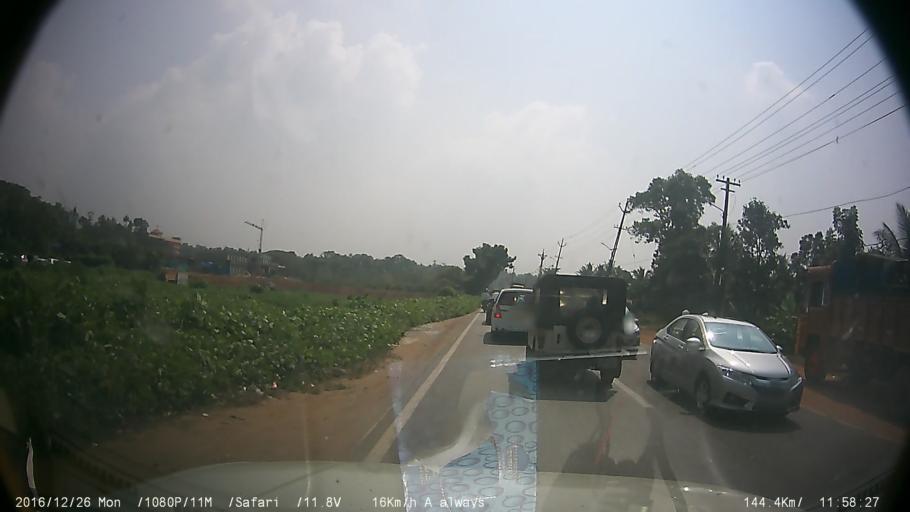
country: IN
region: Kerala
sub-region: Kottayam
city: Changanacheri
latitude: 9.4500
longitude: 76.5470
